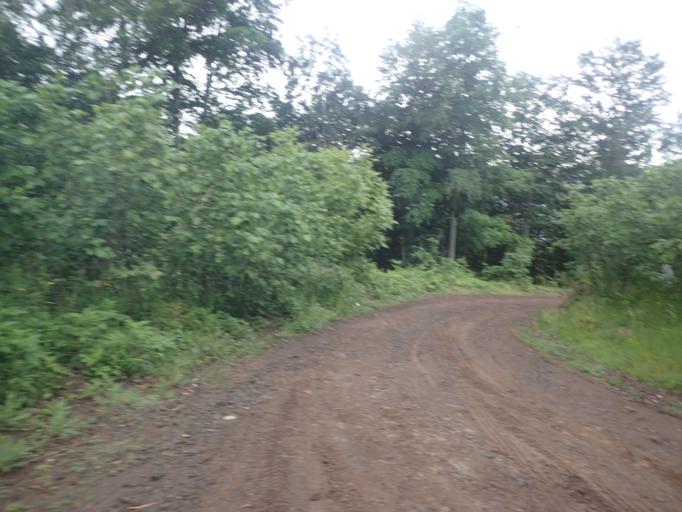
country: TR
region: Samsun
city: Salipazari
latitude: 40.9348
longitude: 36.8653
